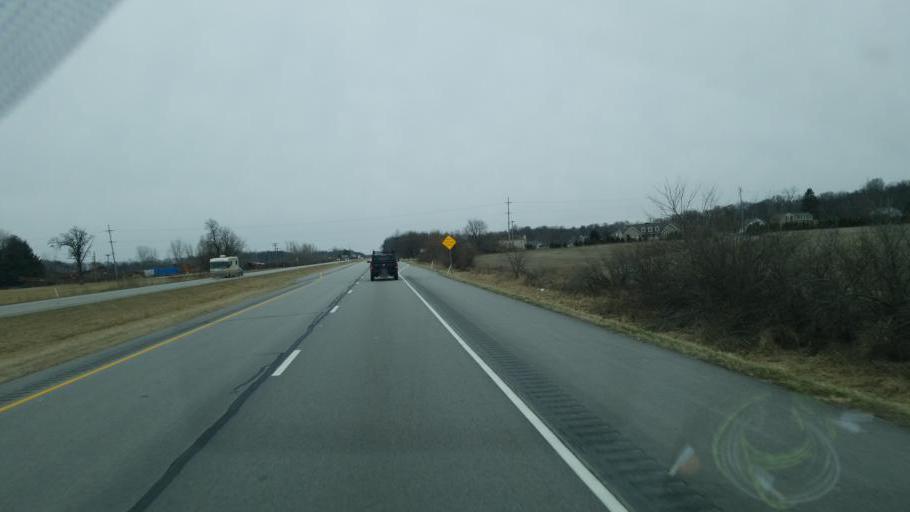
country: US
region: Indiana
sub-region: Marshall County
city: Plymouth
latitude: 41.3201
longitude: -86.2758
